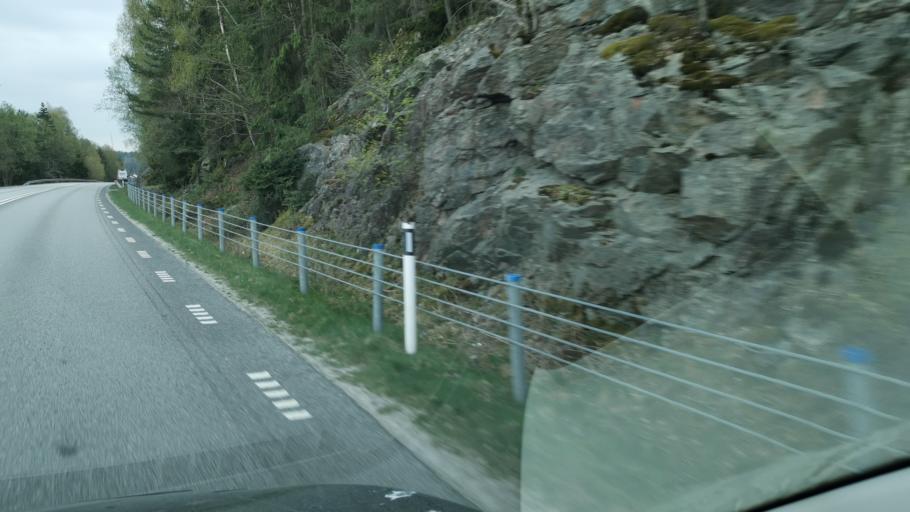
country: SE
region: Vaestra Goetaland
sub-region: Orust
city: Henan
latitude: 58.2147
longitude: 11.6913
